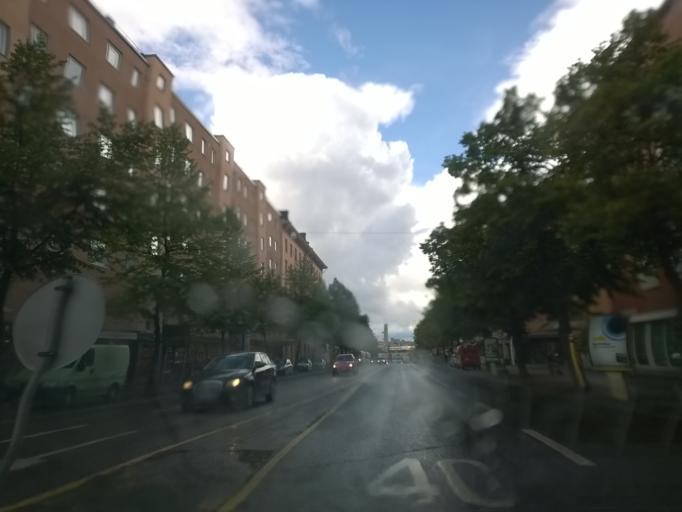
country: FI
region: Pirkanmaa
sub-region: Tampere
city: Tampere
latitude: 61.4990
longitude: 23.7831
